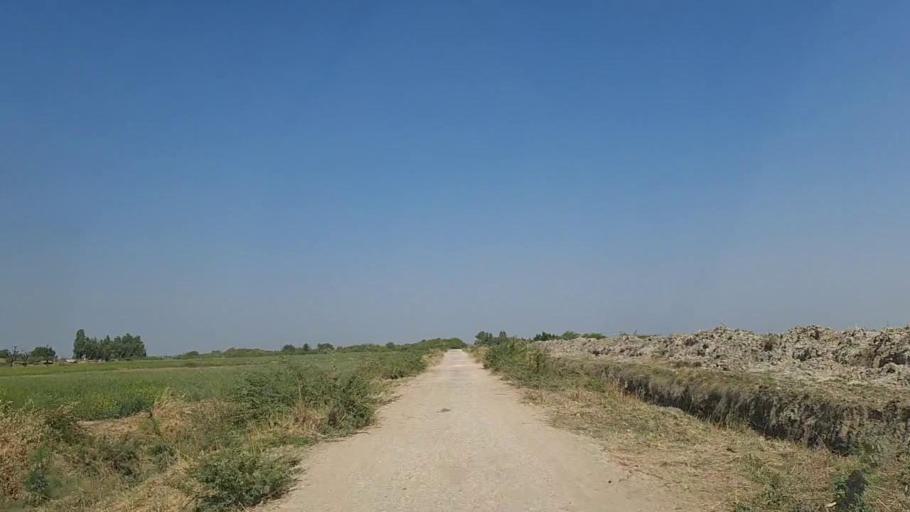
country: PK
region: Sindh
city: Digri
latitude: 25.1882
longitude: 69.1449
